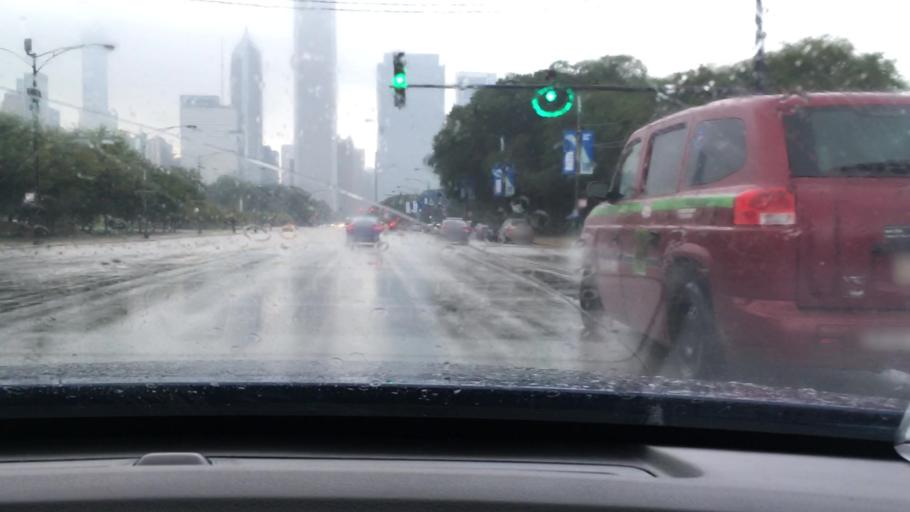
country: US
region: Illinois
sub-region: Cook County
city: Chicago
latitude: 41.8732
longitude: -87.6205
